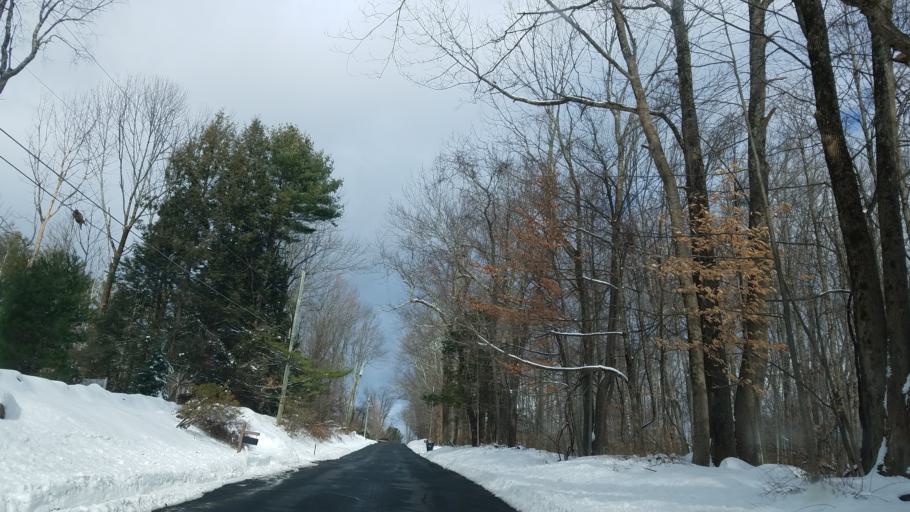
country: US
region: Connecticut
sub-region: Litchfield County
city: Winsted
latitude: 41.9680
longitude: -73.0754
